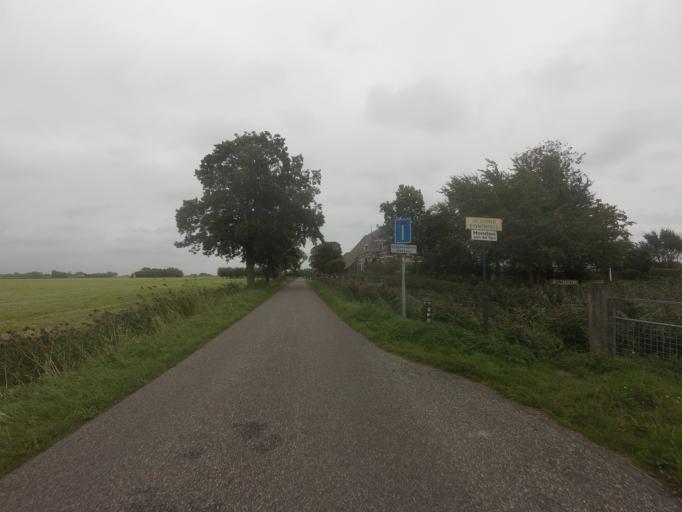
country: NL
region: Friesland
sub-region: Gemeente Leeuwarden
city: Bilgaard
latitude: 53.2280
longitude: 5.7823
